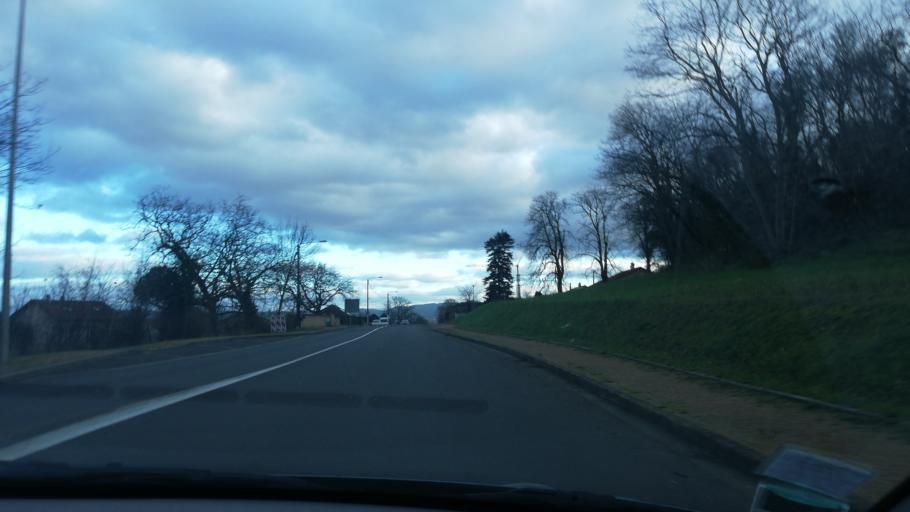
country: FR
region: Auvergne
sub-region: Departement du Puy-de-Dome
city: Vertaizon
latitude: 45.7714
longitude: 3.2968
